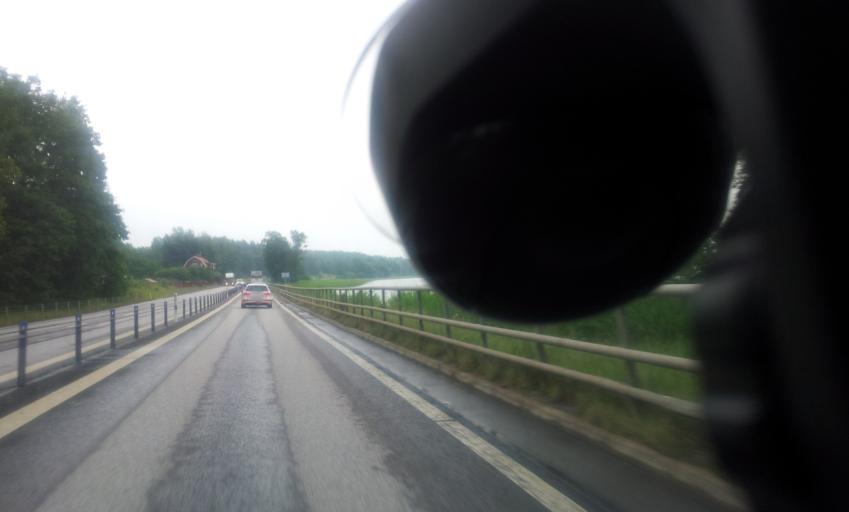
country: SE
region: Kalmar
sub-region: Vasterviks Kommun
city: Gamleby
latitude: 57.8056
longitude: 16.5017
